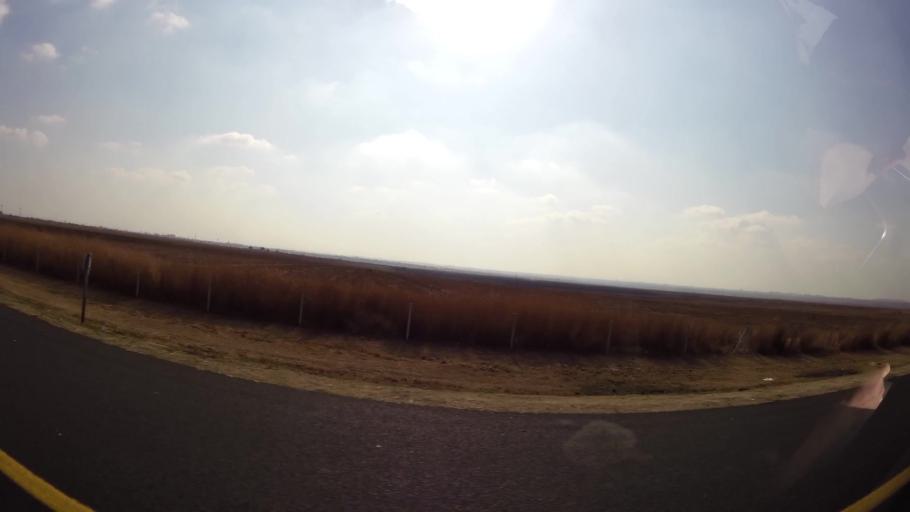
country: ZA
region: Gauteng
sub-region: Ekurhuleni Metropolitan Municipality
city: Springs
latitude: -26.1591
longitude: 28.4358
